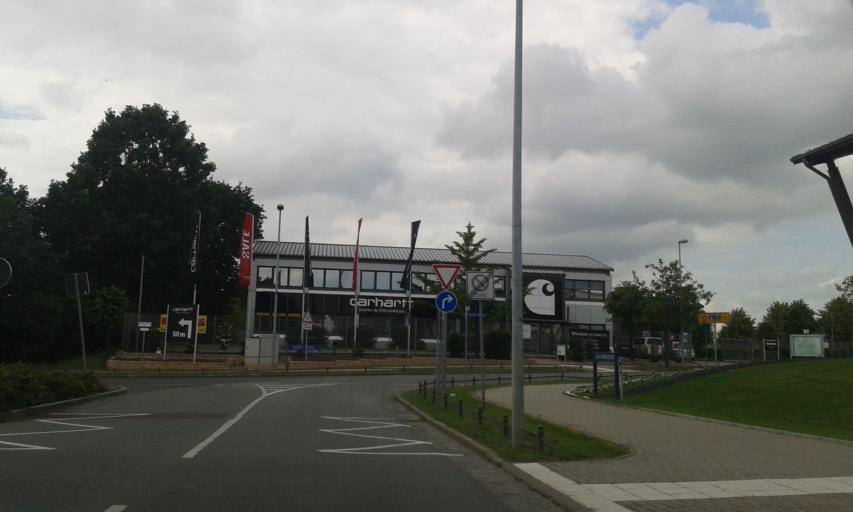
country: DE
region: Brandenburg
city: Wustermark
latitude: 52.5403
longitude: 12.9783
